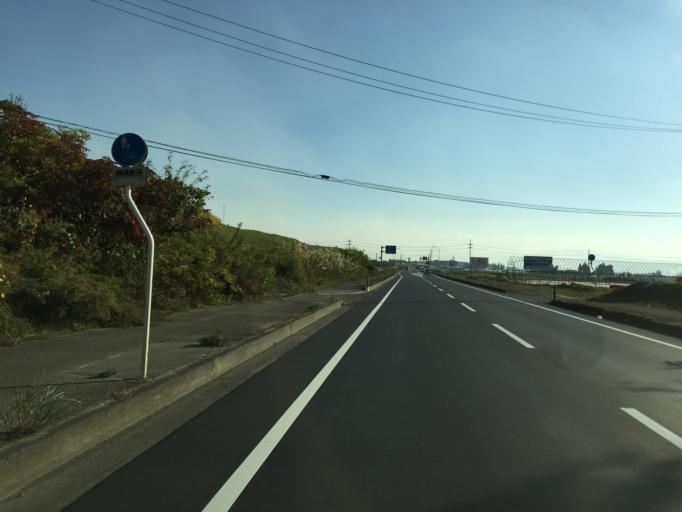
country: JP
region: Fukushima
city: Kitakata
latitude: 37.6851
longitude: 139.8895
